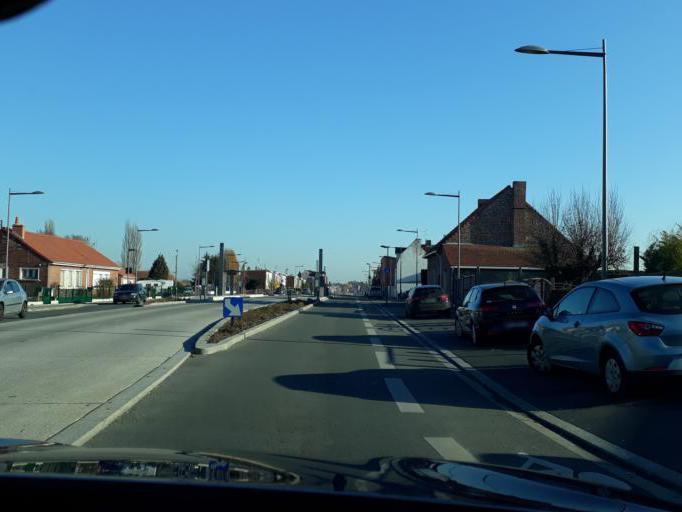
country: FR
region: Nord-Pas-de-Calais
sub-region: Departement du Nord
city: Ecaillon
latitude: 50.3357
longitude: 3.2115
